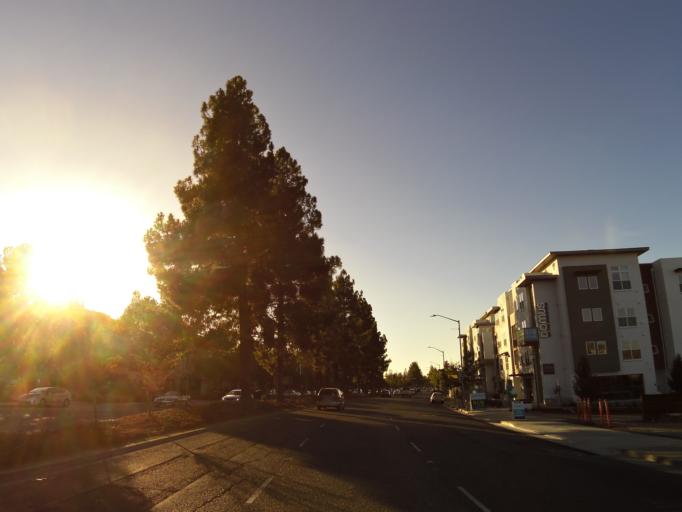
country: US
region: California
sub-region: Santa Clara County
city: Los Altos
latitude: 37.4022
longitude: -122.1152
